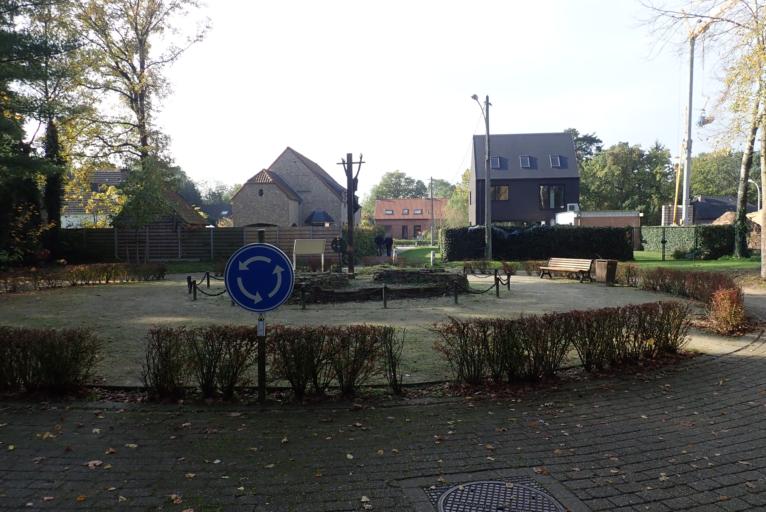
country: BE
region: Flanders
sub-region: Provincie Antwerpen
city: Zoersel
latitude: 51.2762
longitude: 4.7108
